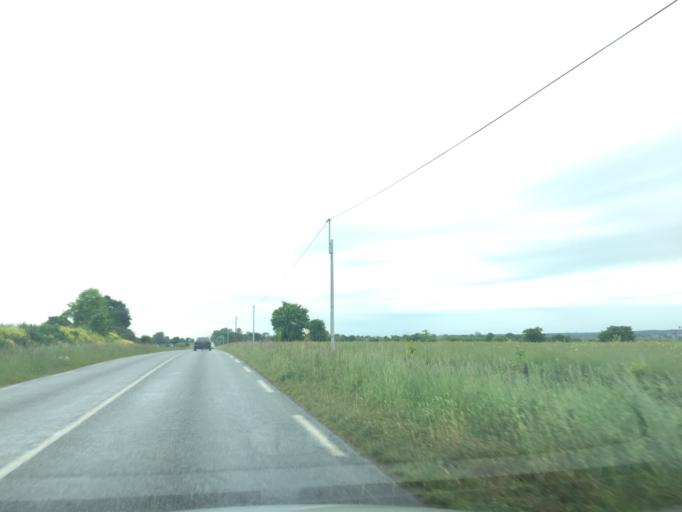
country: FR
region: Brittany
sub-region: Departement des Cotes-d'Armor
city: Crehen
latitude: 48.5563
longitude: -2.1923
